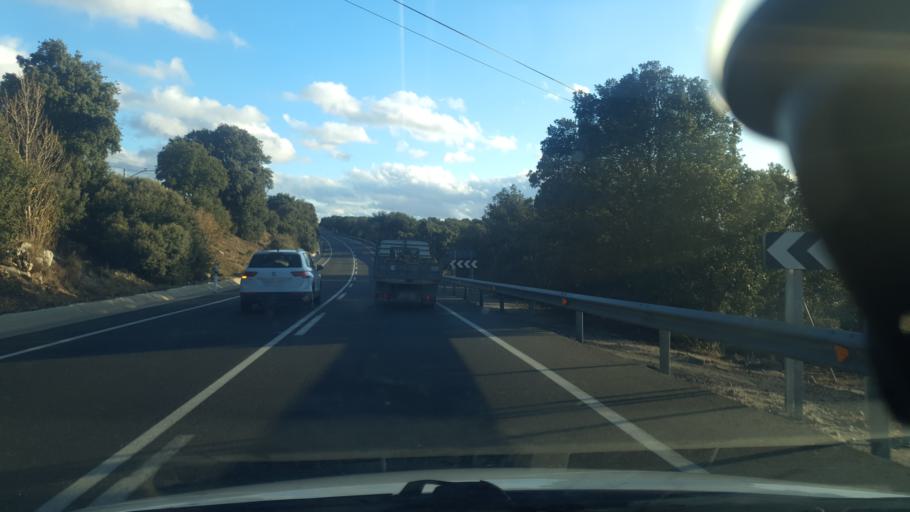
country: ES
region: Castille and Leon
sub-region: Provincia de Avila
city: Mingorria
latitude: 40.7157
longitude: -4.6743
